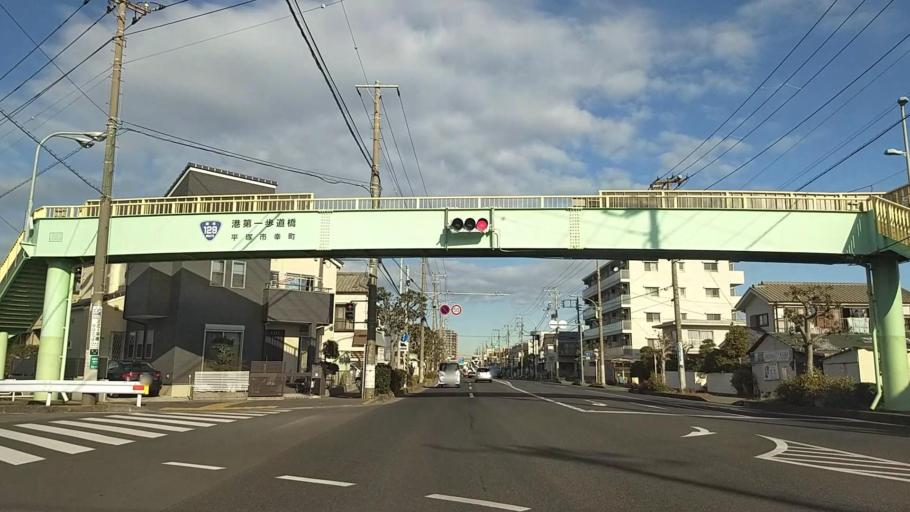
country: JP
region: Kanagawa
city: Hiratsuka
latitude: 35.3189
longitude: 139.3616
